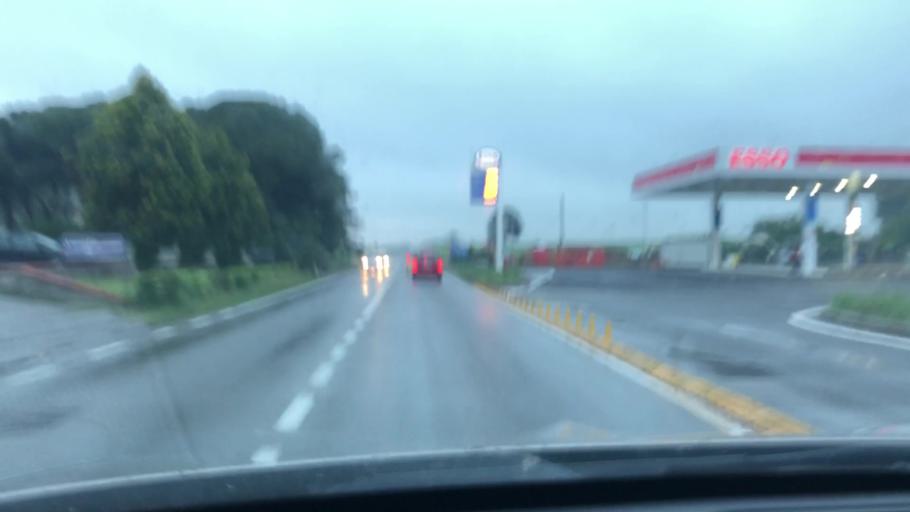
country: IT
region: Tuscany
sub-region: Province of Pisa
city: Val di Cava
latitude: 43.6411
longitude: 10.6504
